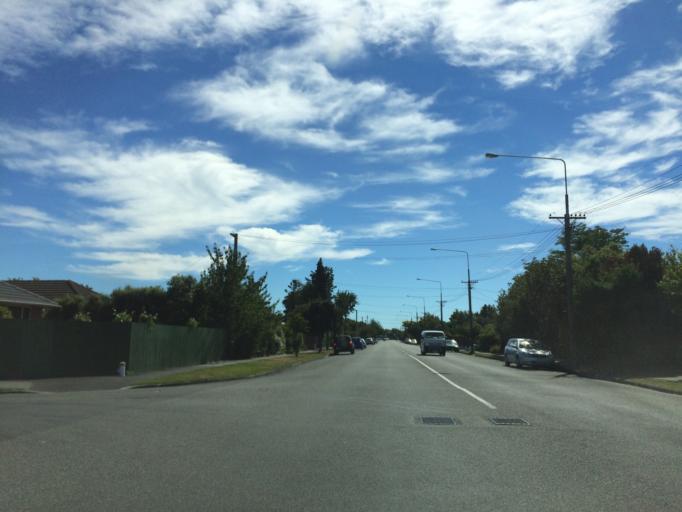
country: NZ
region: Canterbury
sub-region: Christchurch City
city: Christchurch
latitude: -43.5034
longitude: 172.5827
